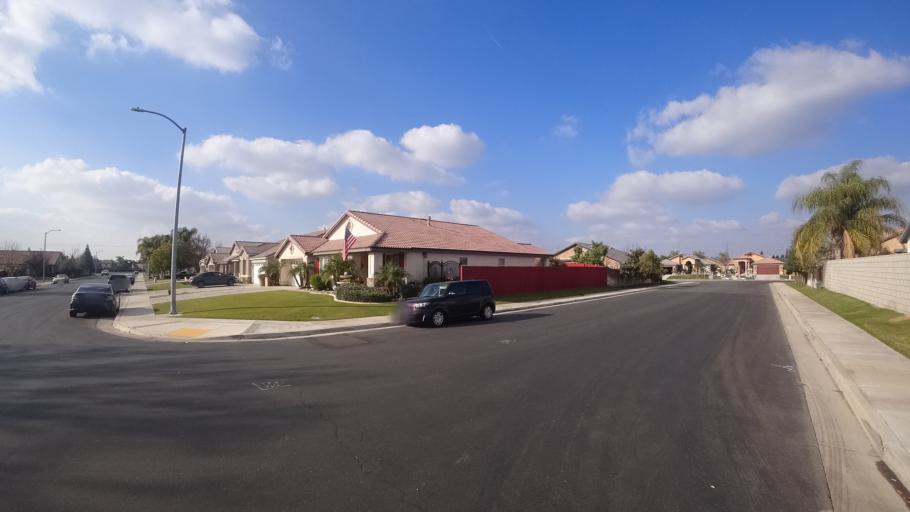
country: US
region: California
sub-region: Kern County
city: Greenacres
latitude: 35.3067
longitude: -119.1073
